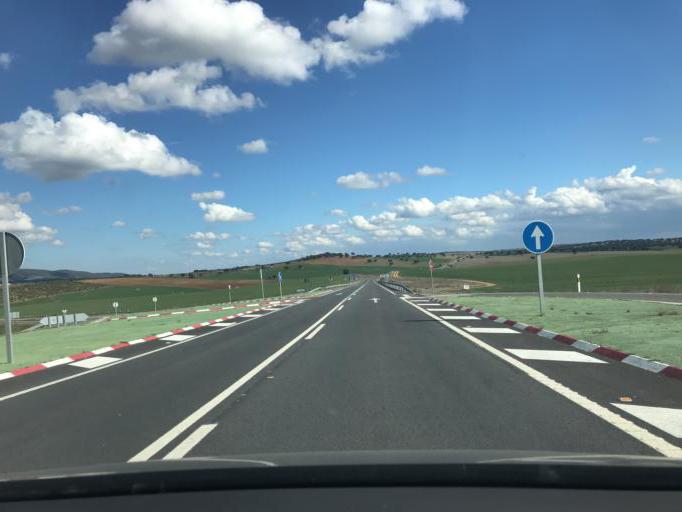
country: ES
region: Extremadura
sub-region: Provincia de Badajoz
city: Granja de Torrehermosa
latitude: 38.2981
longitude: -5.5585
